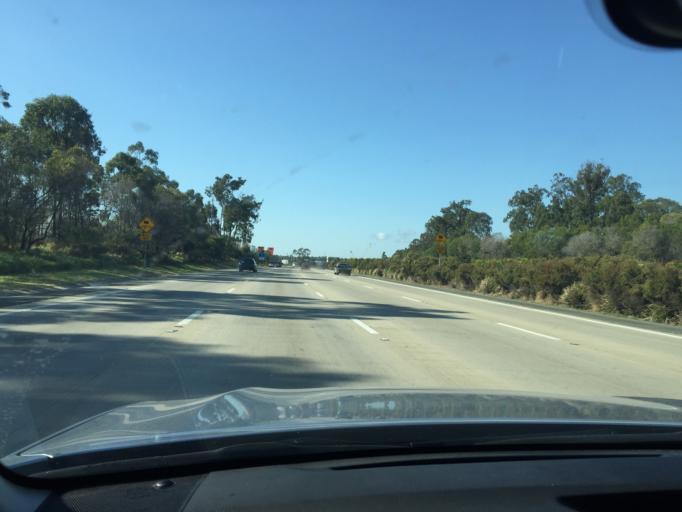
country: AU
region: Queensland
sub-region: Gold Coast
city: Ormeau Hills
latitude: -27.7652
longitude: 153.2491
